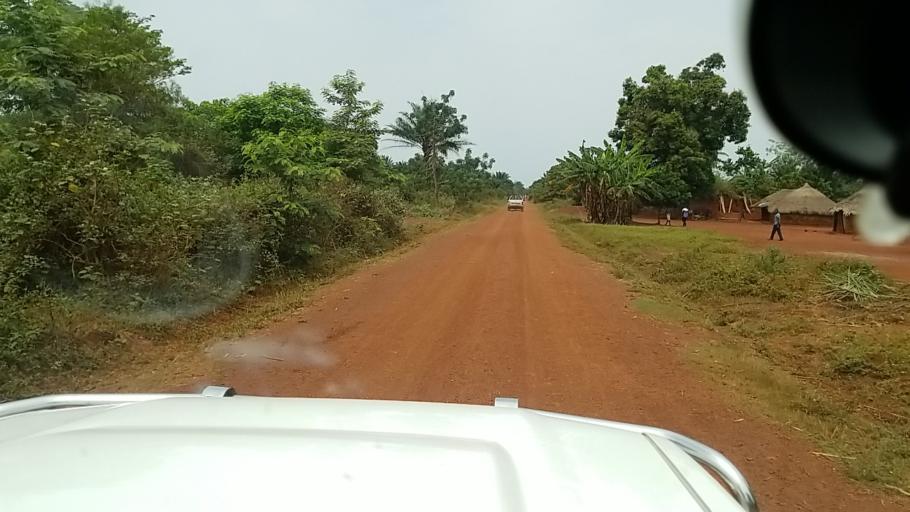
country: CD
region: Equateur
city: Gemena
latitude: 3.5228
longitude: 19.3641
